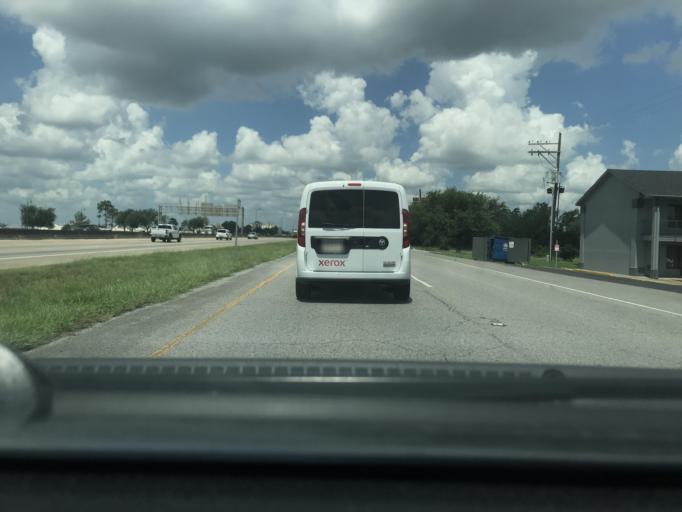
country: US
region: Louisiana
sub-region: Calcasieu Parish
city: Westlake
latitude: 30.2374
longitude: -93.2304
